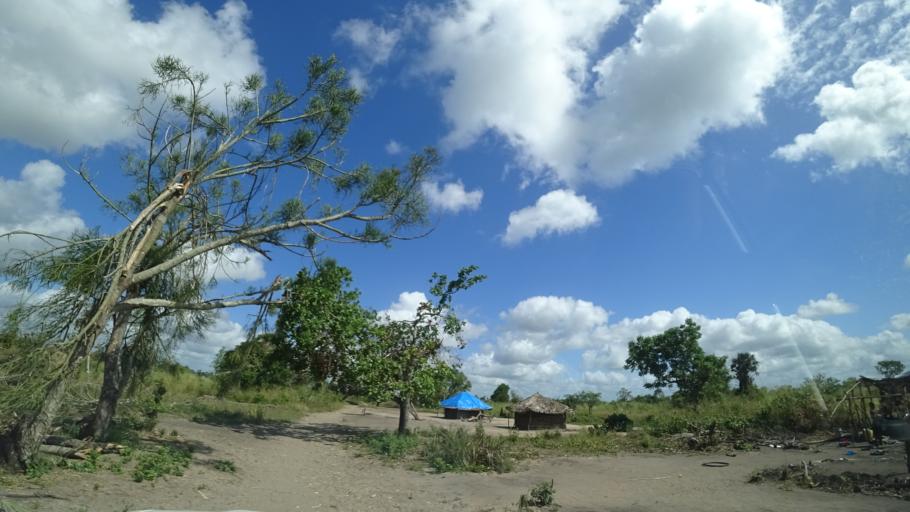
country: MZ
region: Sofala
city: Dondo
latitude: -19.3570
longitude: 34.5810
